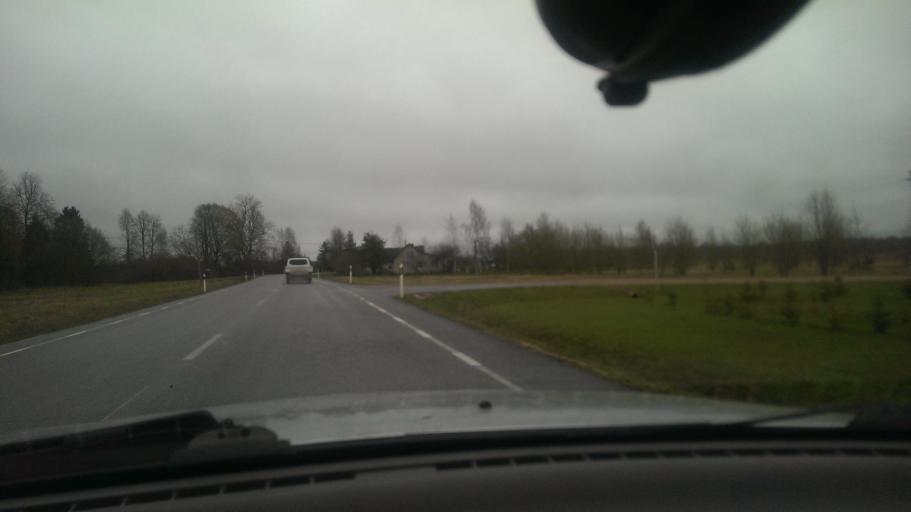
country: EE
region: Tartu
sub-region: Tartu linn
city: Tartu
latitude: 58.3875
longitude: 26.7958
